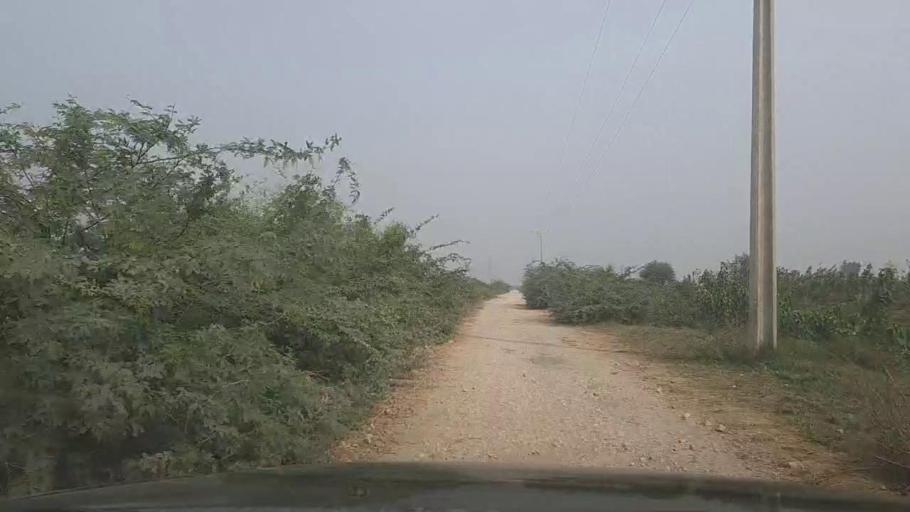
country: PK
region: Sindh
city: Mirpur Sakro
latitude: 24.5691
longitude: 67.7885
